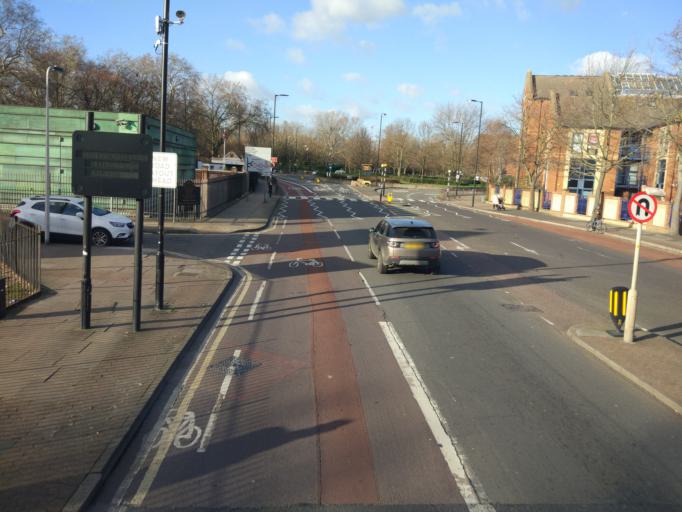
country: GB
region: England
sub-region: Greater London
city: Bethnal Green
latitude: 51.4979
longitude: -0.0546
